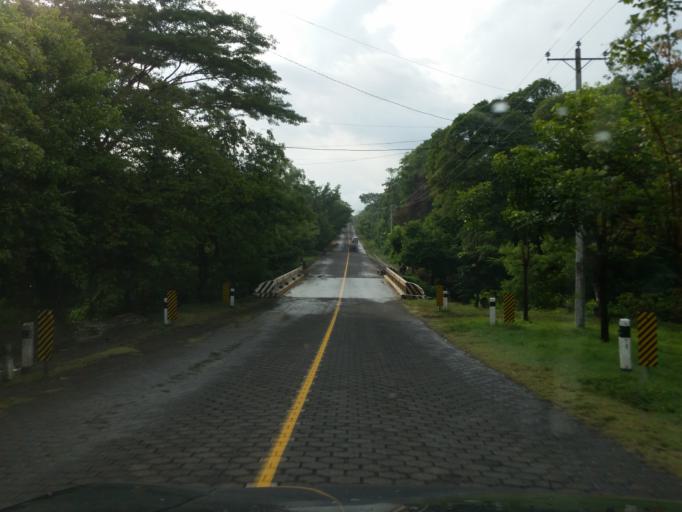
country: NI
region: Managua
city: Masachapa
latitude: 11.8260
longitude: -86.5013
